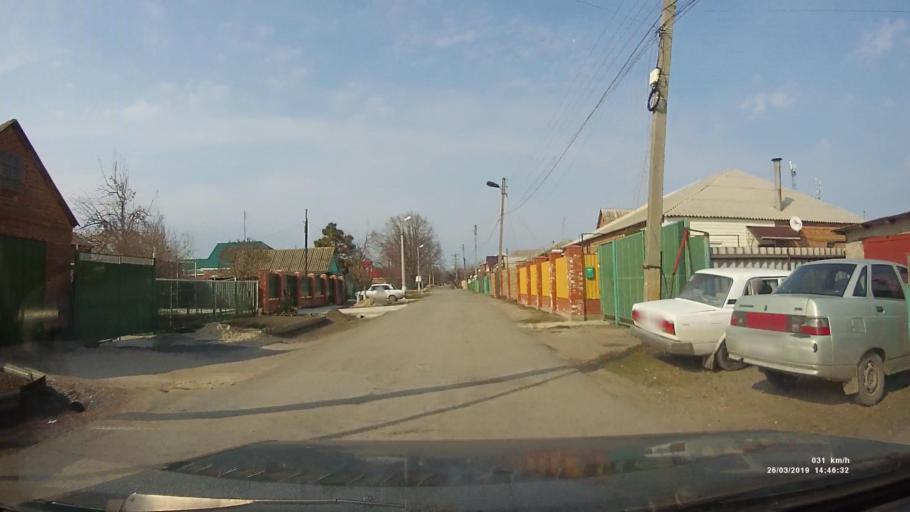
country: RU
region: Rostov
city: Novobessergenovka
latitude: 47.1870
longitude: 38.8603
